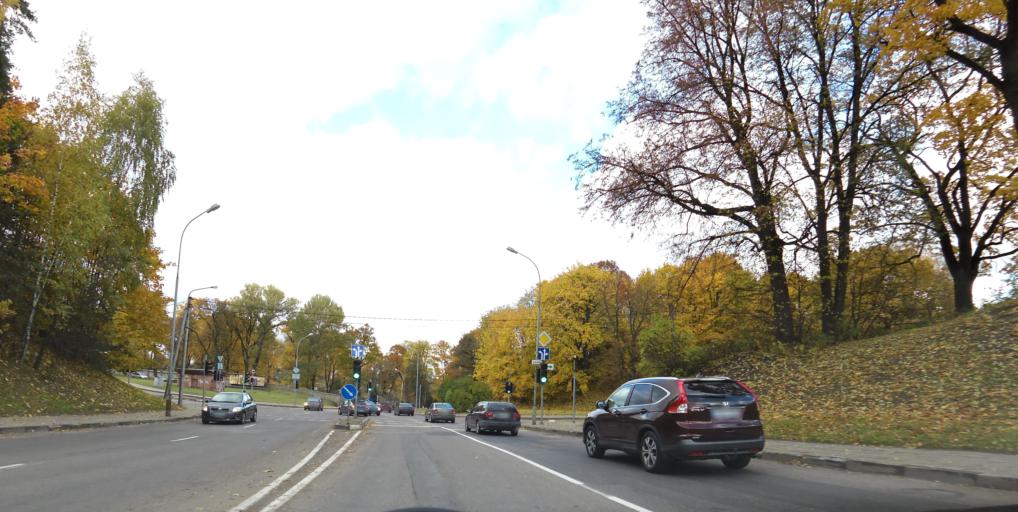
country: LT
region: Vilnius County
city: Rasos
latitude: 54.6661
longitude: 25.3055
